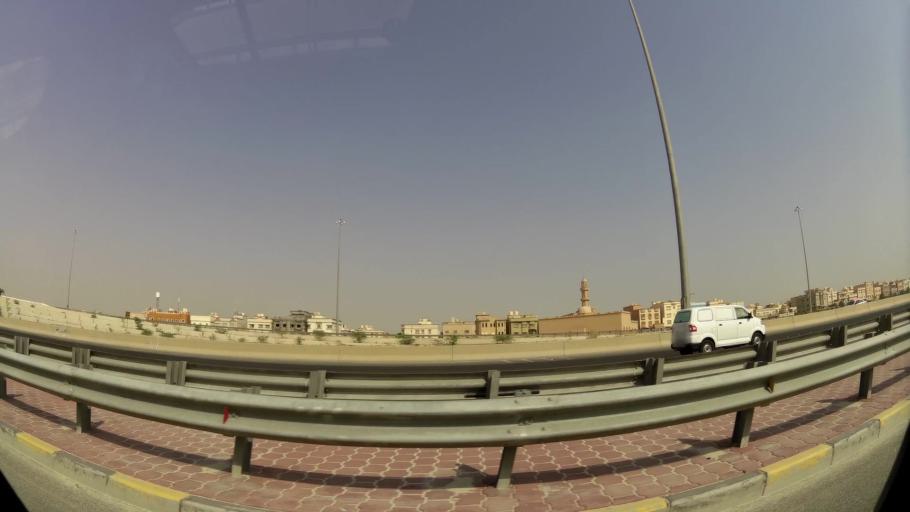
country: KW
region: Muhafazat al Jahra'
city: Al Jahra'
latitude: 29.2985
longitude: 47.7165
